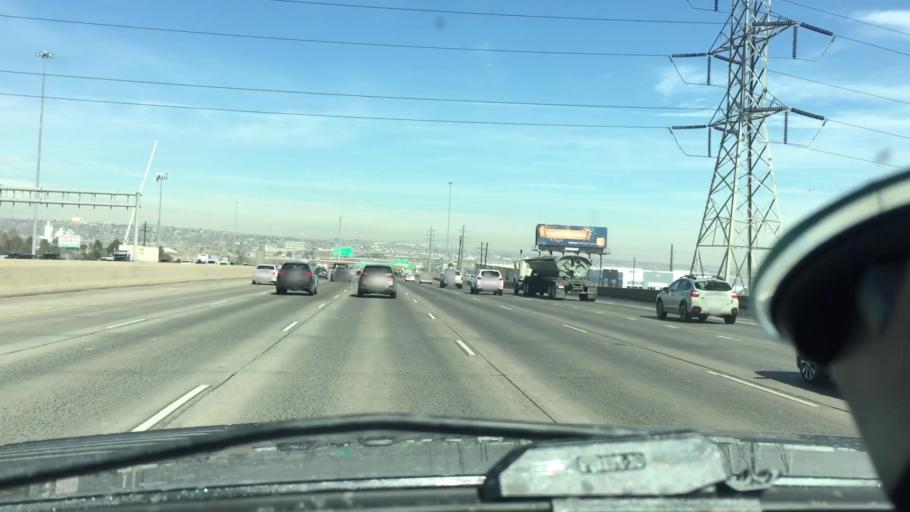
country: US
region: Colorado
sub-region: Adams County
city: Twin Lakes
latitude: 39.8081
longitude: -104.9825
